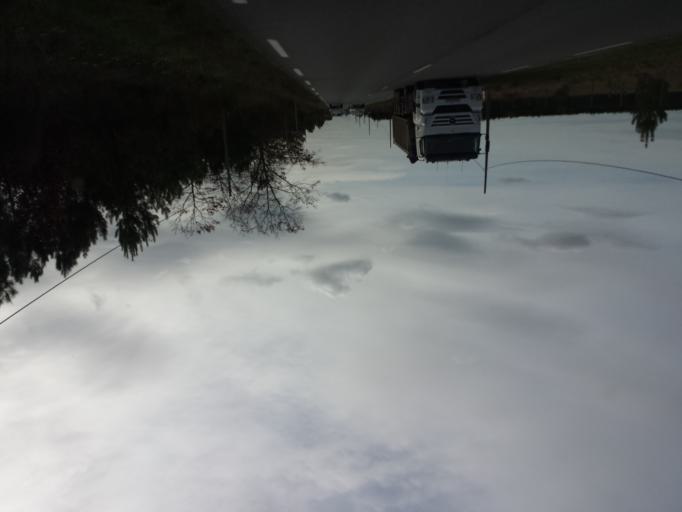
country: FR
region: Aquitaine
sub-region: Departement de la Gironde
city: Marcheprime
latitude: 44.7747
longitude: -0.9287
